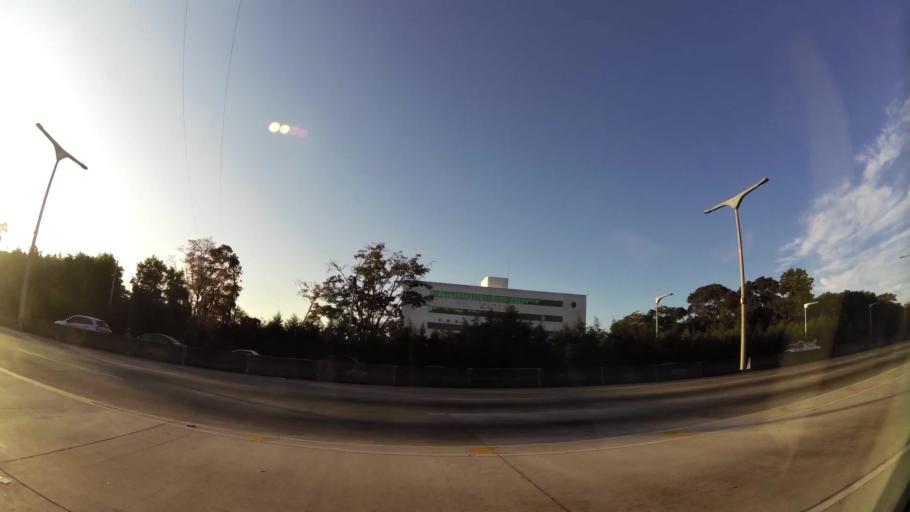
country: SV
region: La Libertad
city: Santa Tecla
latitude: 13.6852
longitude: -89.2603
